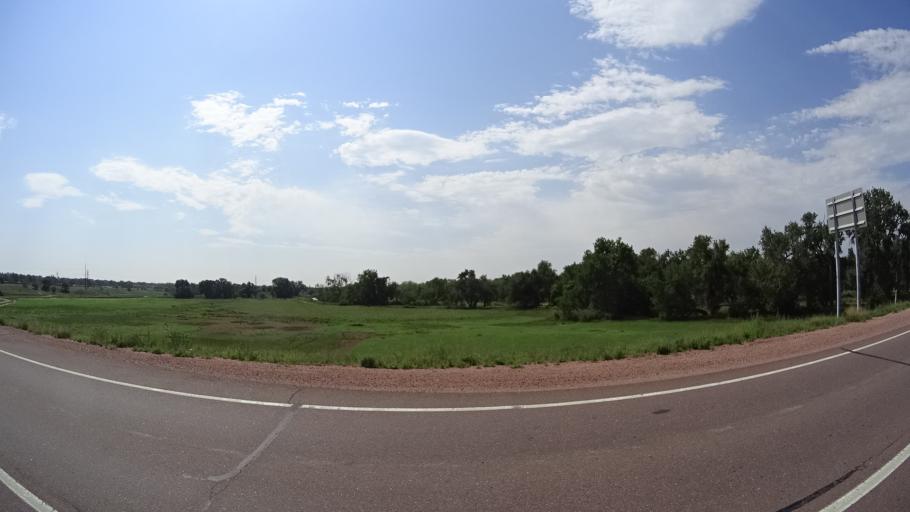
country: US
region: Colorado
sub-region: El Paso County
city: Stratmoor
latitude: 38.7653
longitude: -104.7638
